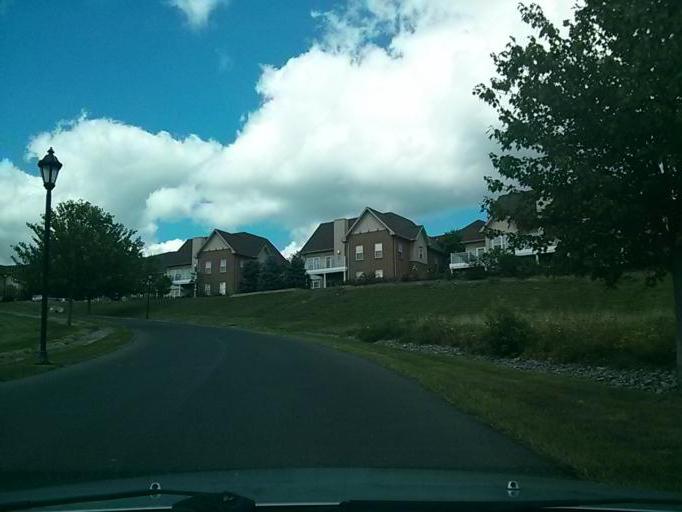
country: US
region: Pennsylvania
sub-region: Centre County
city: State College
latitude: 40.8236
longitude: -77.8715
